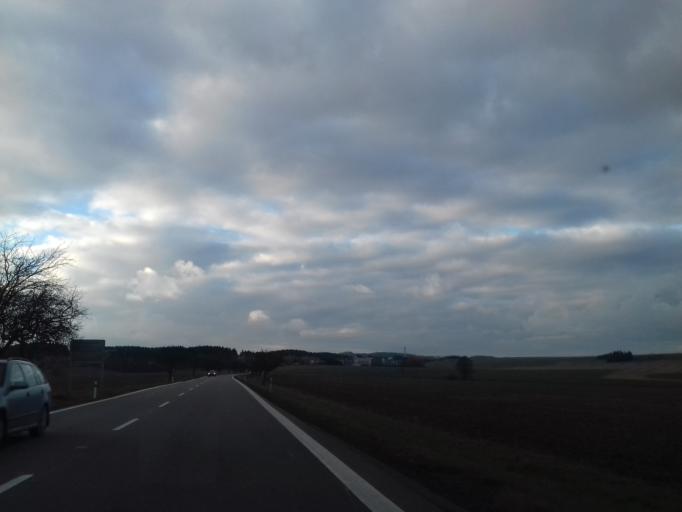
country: CZ
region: Pardubicky
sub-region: Okres Svitavy
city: Policka
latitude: 49.7178
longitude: 16.2439
